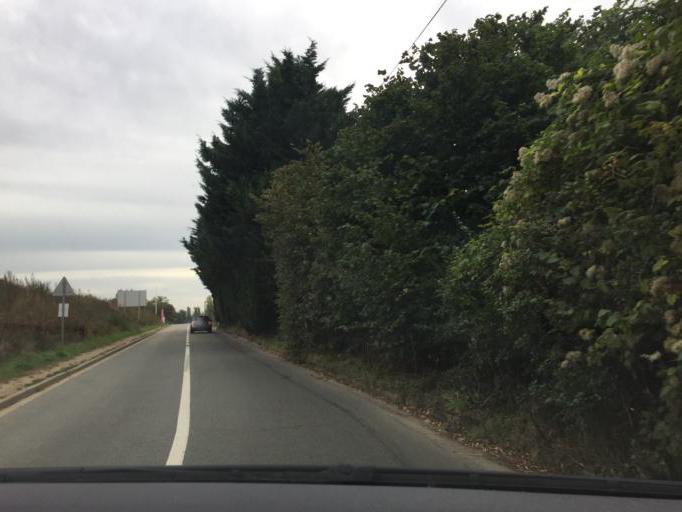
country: FR
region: Ile-de-France
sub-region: Departement des Yvelines
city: Les Loges-en-Josas
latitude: 48.7605
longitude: 2.1246
